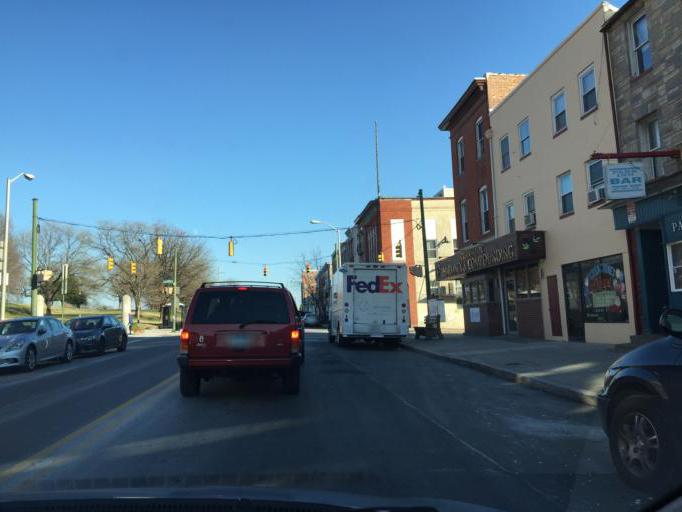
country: US
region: Maryland
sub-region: City of Baltimore
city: Baltimore
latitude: 39.2859
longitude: -76.5848
